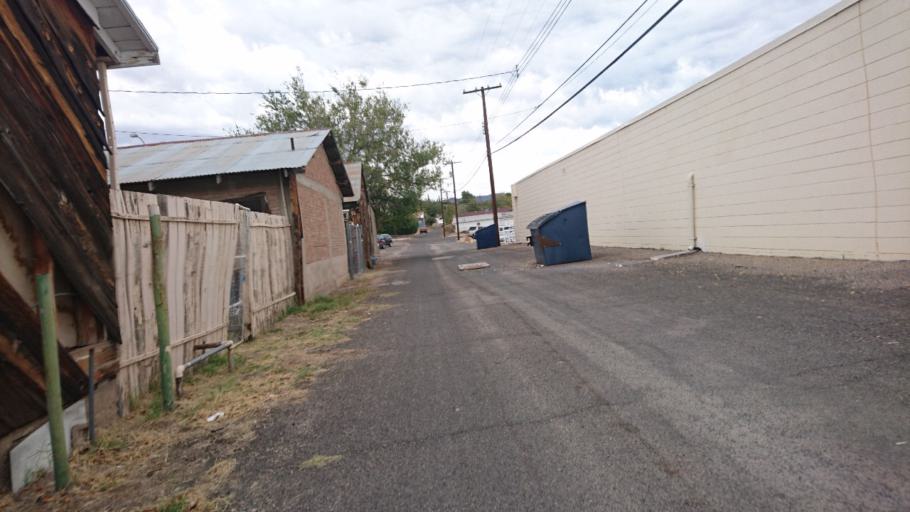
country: US
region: Arizona
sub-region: Mohave County
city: Kingman
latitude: 35.1899
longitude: -114.0503
